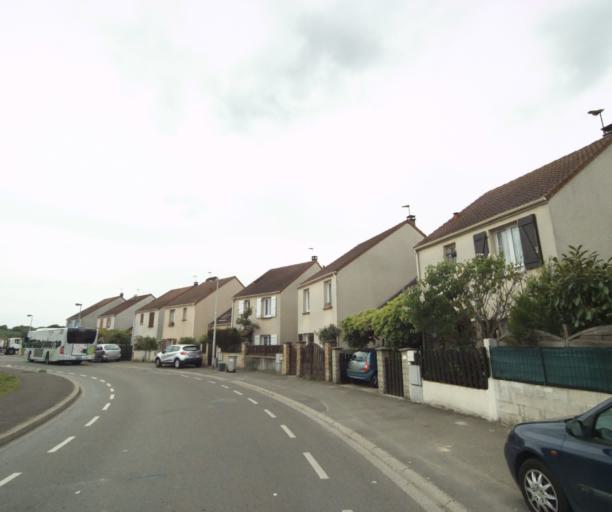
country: FR
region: Ile-de-France
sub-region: Departement des Yvelines
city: Bouafle
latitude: 48.9744
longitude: 1.9122
